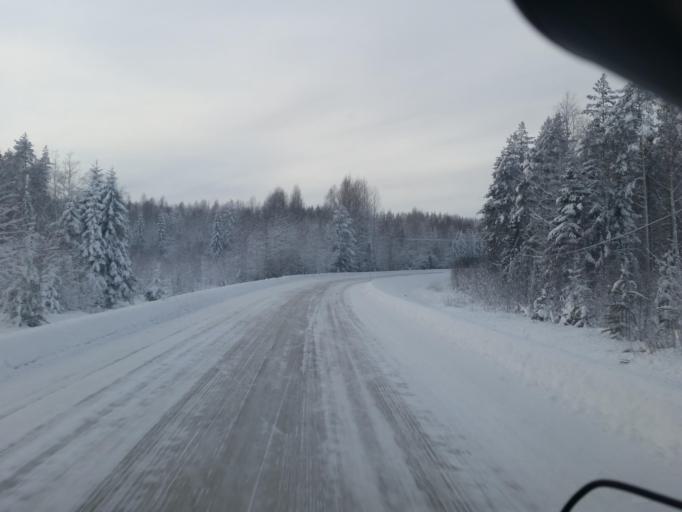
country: SE
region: Norrbotten
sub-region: Pitea Kommun
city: Norrfjarden
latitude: 65.5201
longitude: 21.4382
